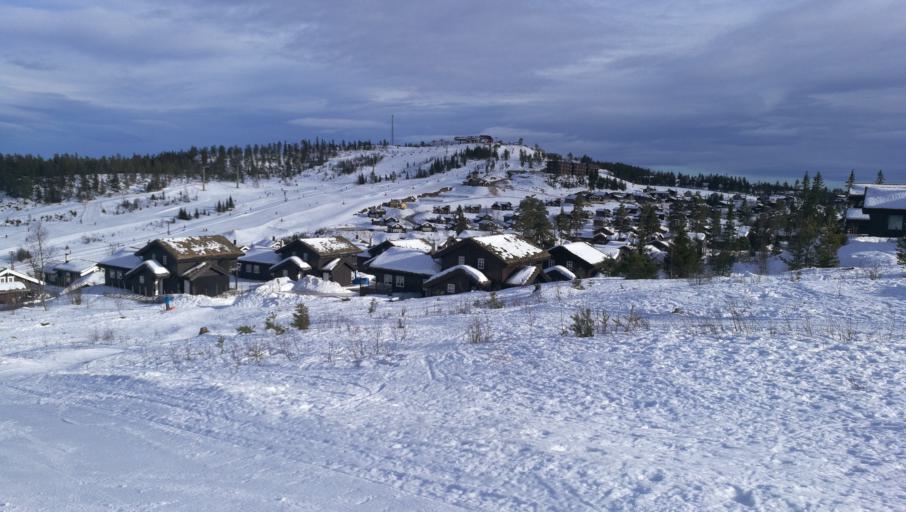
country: SE
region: Vaermland
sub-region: Torsby Kommun
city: Torsby
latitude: 60.6573
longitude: 12.9319
